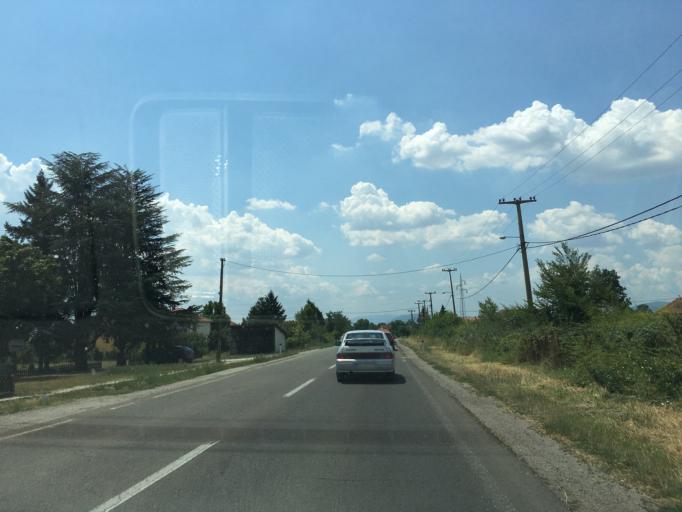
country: RS
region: Central Serbia
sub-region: Belgrade
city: Mladenovac
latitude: 44.4141
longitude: 20.6790
